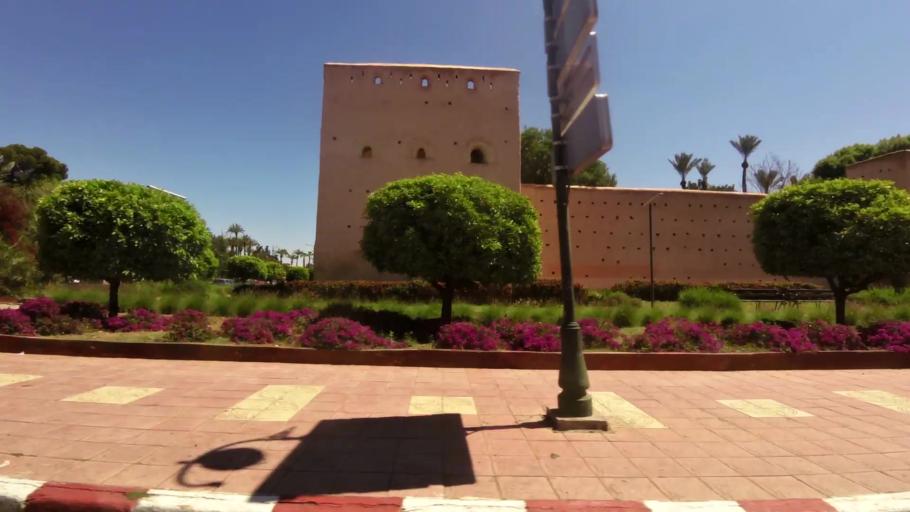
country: MA
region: Marrakech-Tensift-Al Haouz
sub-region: Marrakech
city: Marrakesh
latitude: 31.6276
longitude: -8.0022
